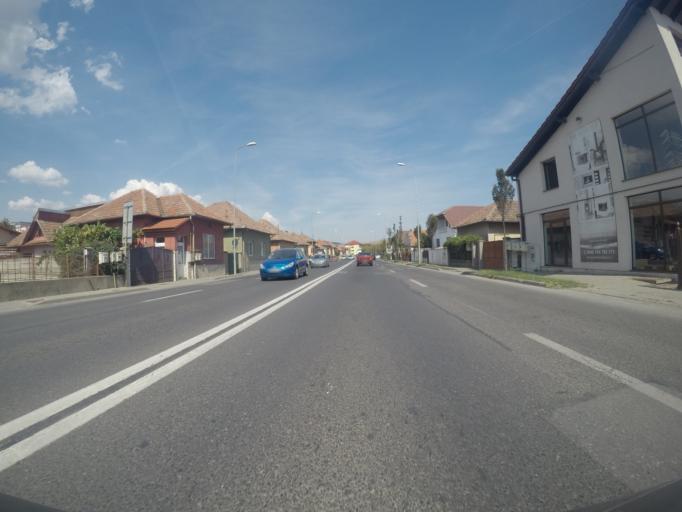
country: RO
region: Alba
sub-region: Municipiul Alba Iulia
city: Barabant
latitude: 46.0837
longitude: 23.5853
